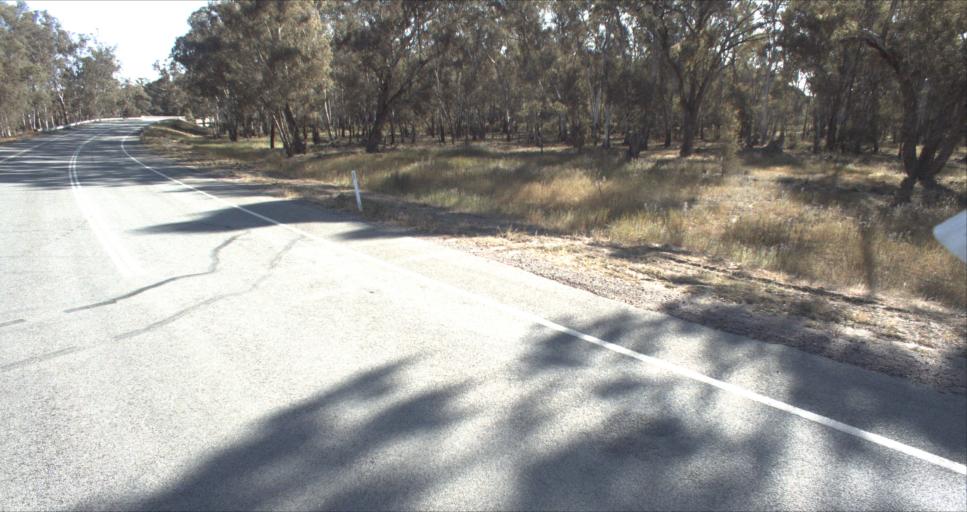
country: AU
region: New South Wales
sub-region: Leeton
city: Leeton
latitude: -34.6371
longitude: 146.3753
